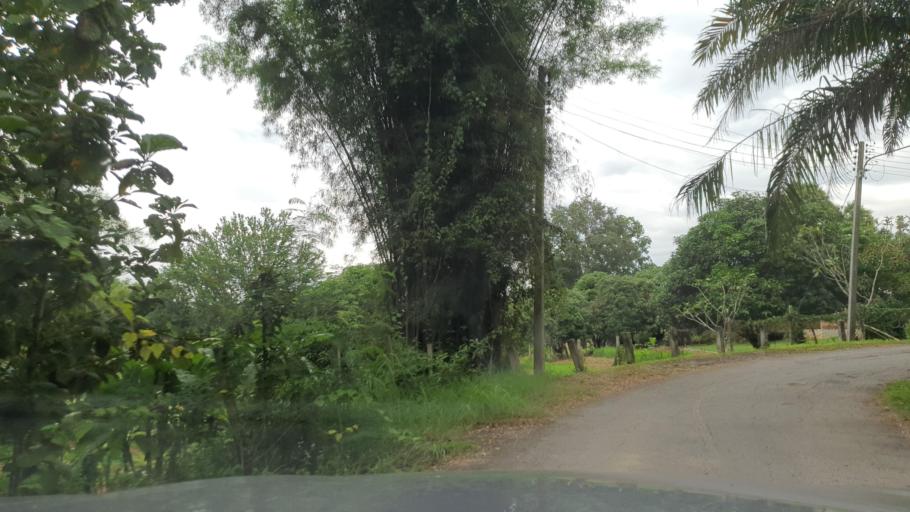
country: TH
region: Chiang Mai
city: Chiang Mai
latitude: 18.9308
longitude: 98.9062
